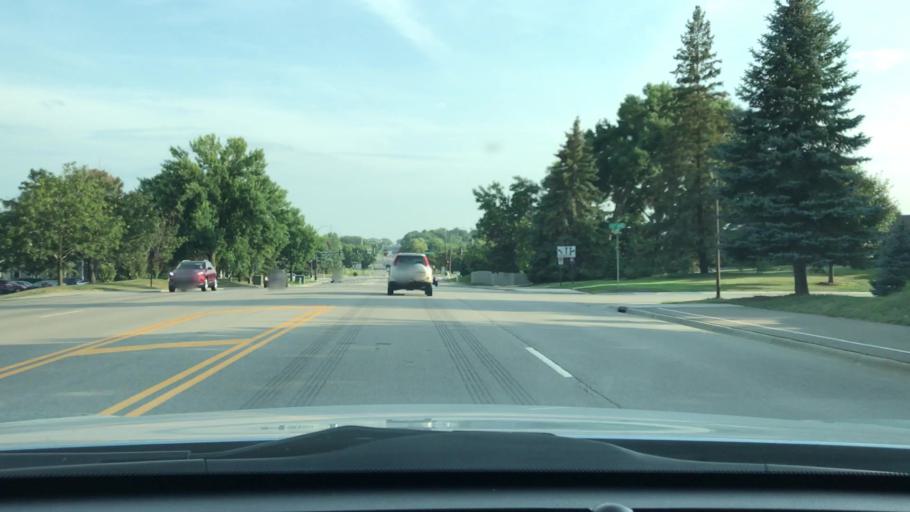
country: US
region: Minnesota
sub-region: Hennepin County
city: Plymouth
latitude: 45.0340
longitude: -93.4818
